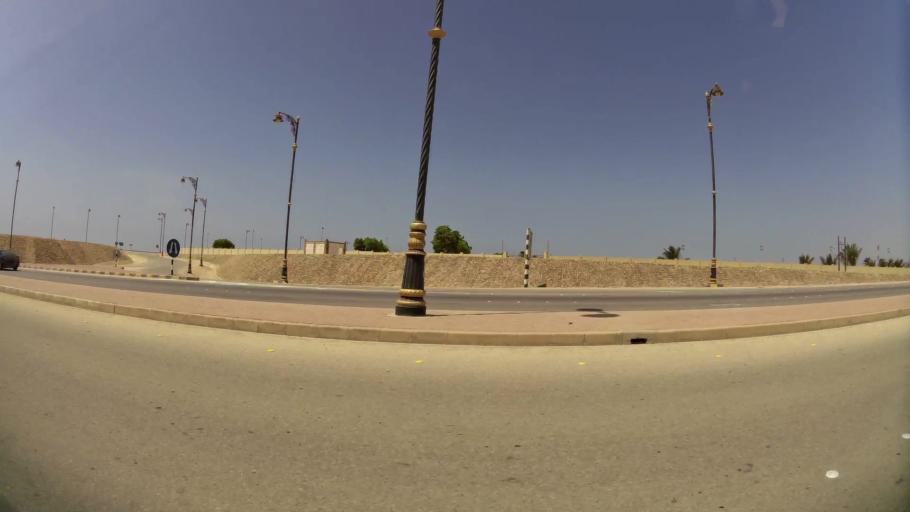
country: OM
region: Zufar
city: Salalah
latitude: 17.0504
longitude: 54.2225
